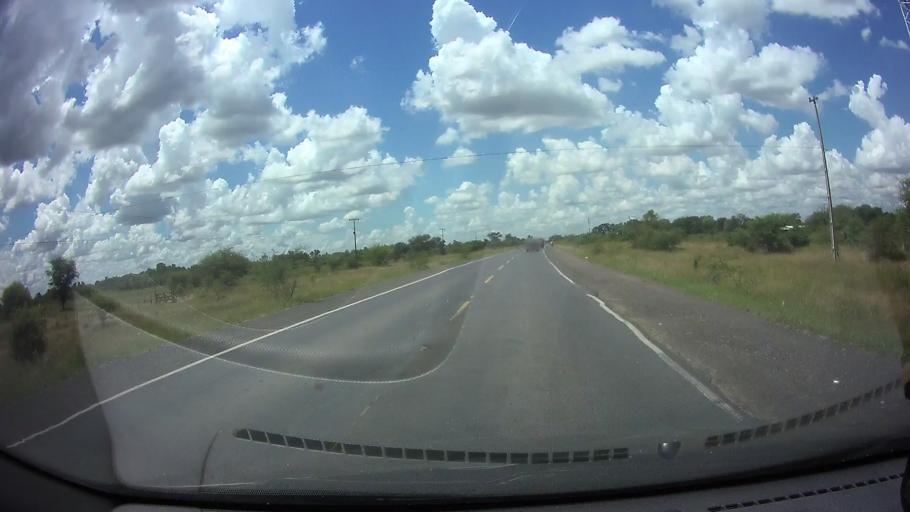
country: PY
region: Presidente Hayes
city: Nanawa
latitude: -25.2245
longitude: -57.6834
